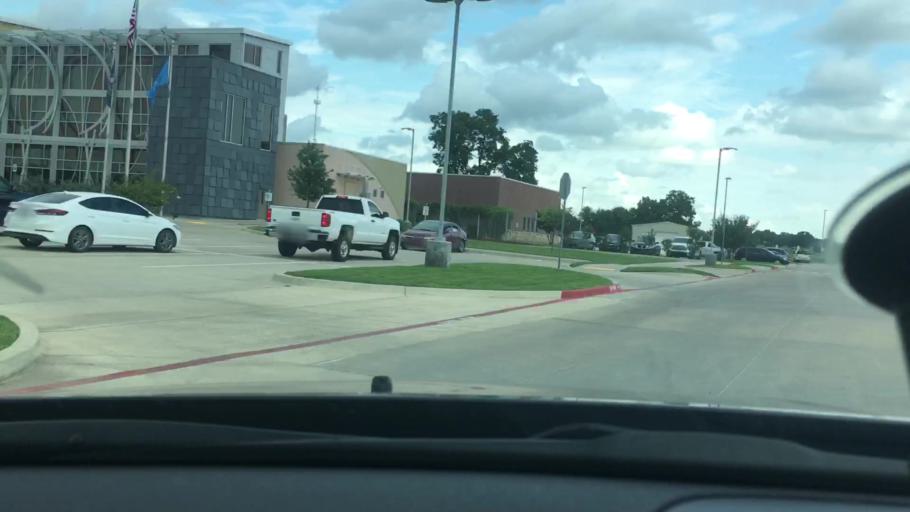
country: US
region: Oklahoma
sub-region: Johnston County
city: Tishomingo
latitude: 34.2337
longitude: -96.6633
